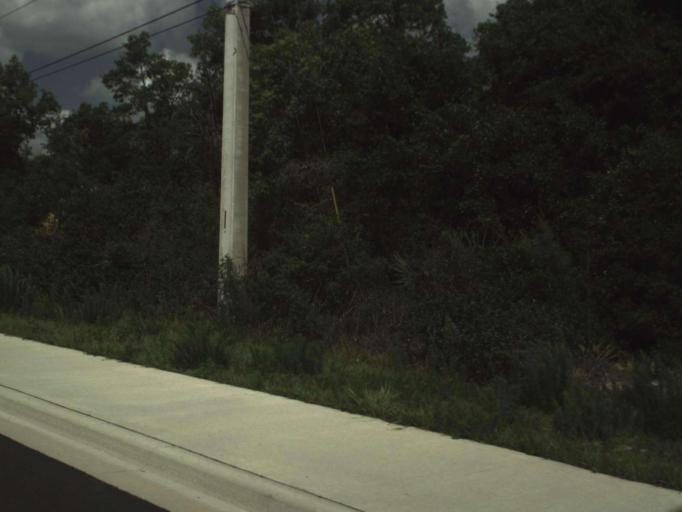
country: US
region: Florida
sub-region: Volusia County
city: Deltona
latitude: 28.8770
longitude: -81.1570
